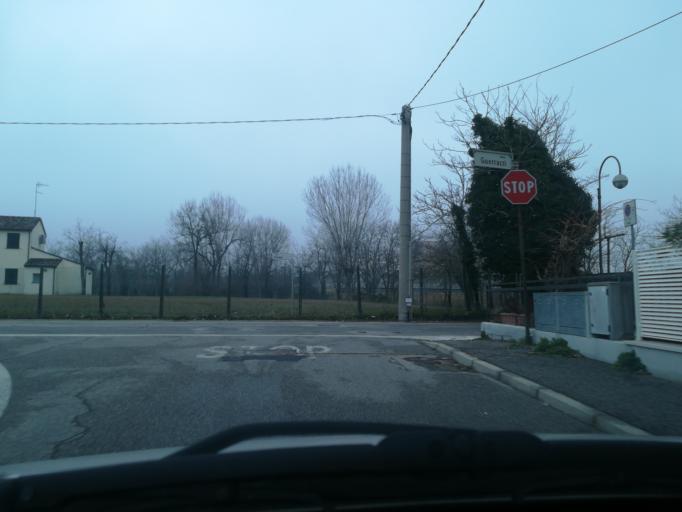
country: IT
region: Emilia-Romagna
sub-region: Provincia di Rimini
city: Riccione
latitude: 44.0185
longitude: 12.6358
